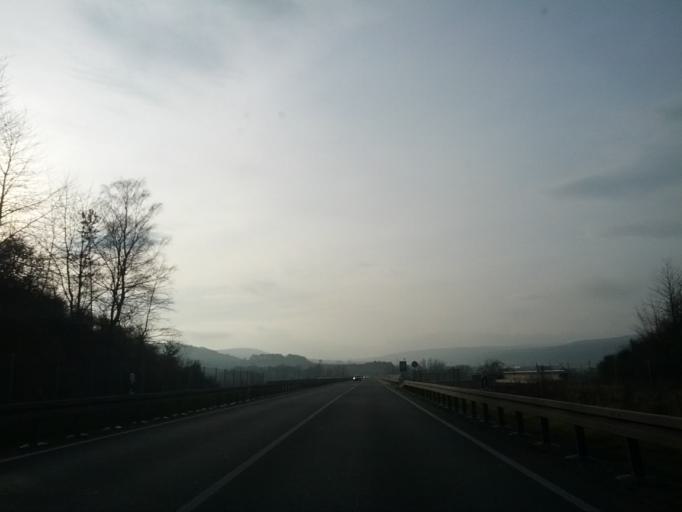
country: DE
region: Thuringia
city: Fambach
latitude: 50.7198
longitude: 10.3693
